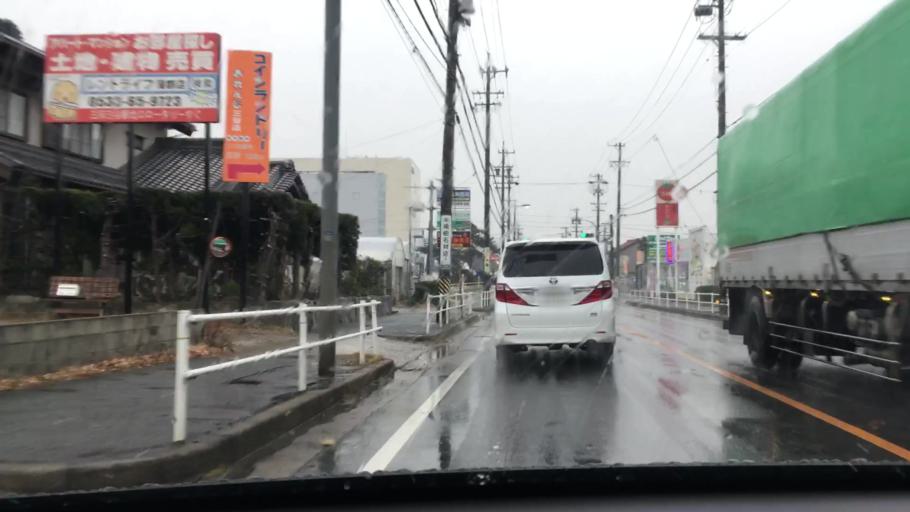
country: JP
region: Aichi
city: Gamagori
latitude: 34.8221
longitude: 137.2371
